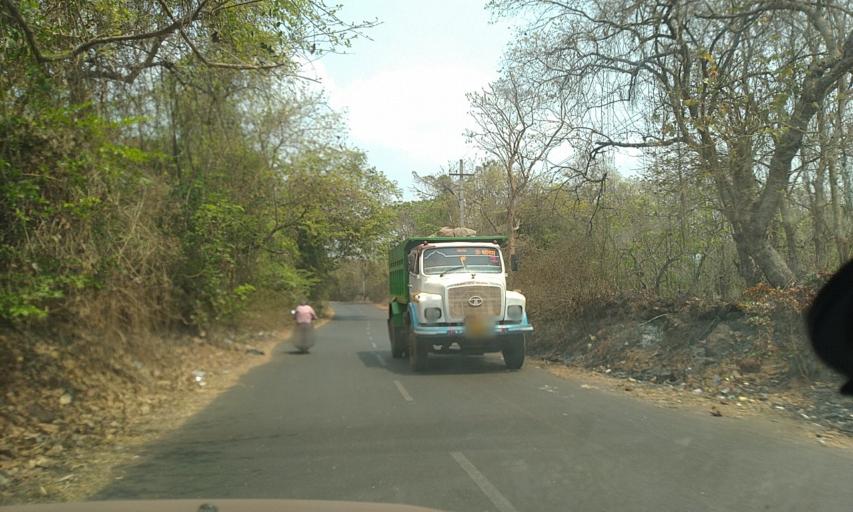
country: IN
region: Goa
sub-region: North Goa
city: Jua
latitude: 15.4931
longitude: 73.9109
